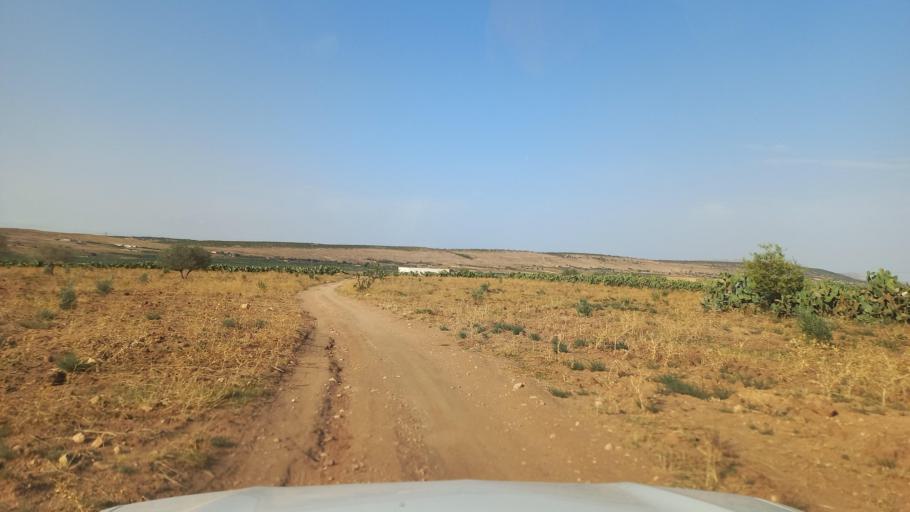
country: TN
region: Al Qasrayn
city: Kasserine
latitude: 35.3474
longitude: 8.8481
